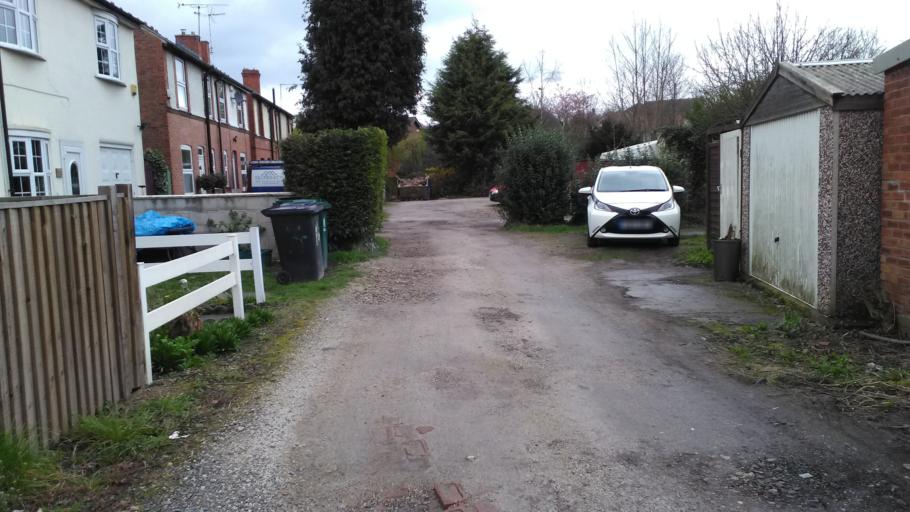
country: GB
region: England
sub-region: Nottinghamshire
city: Radcliffe on Trent
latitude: 52.9714
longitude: -1.0761
